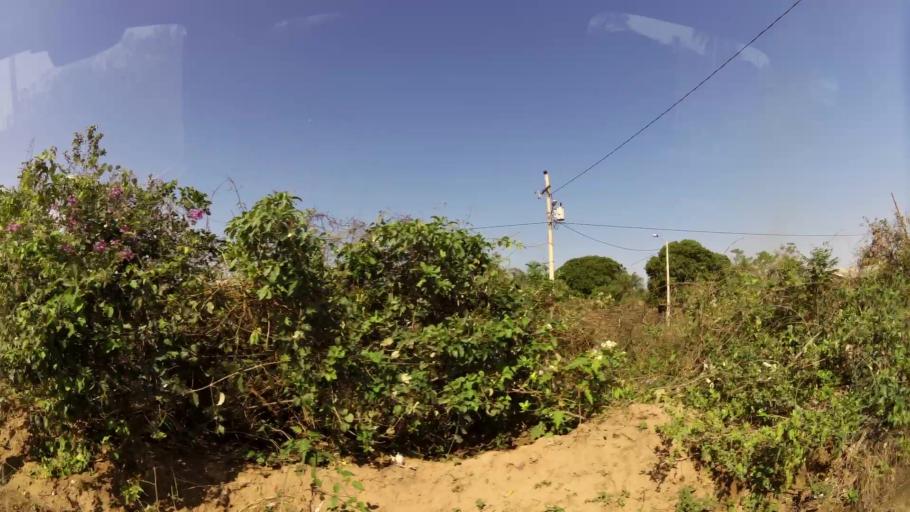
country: BO
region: Santa Cruz
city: Cotoca
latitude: -17.7136
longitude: -63.0639
